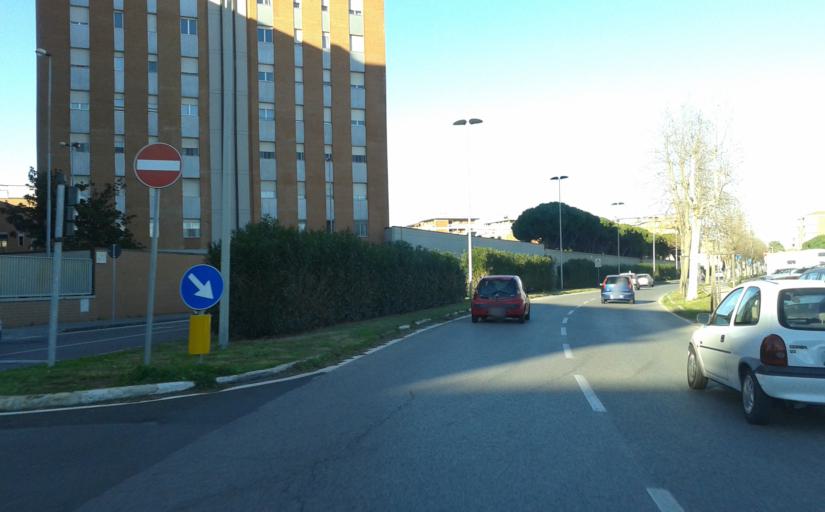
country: IT
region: Tuscany
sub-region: Provincia di Livorno
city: Livorno
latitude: 43.5380
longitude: 10.3226
